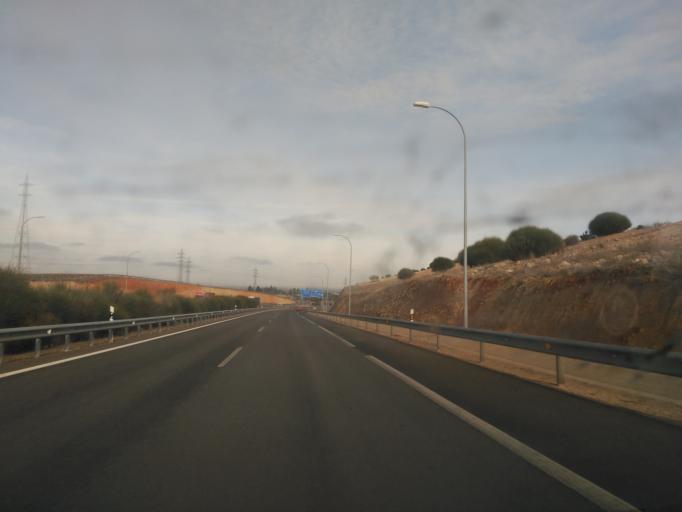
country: ES
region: Castille and Leon
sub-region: Provincia de Salamanca
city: Villamayor
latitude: 40.9917
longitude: -5.6789
